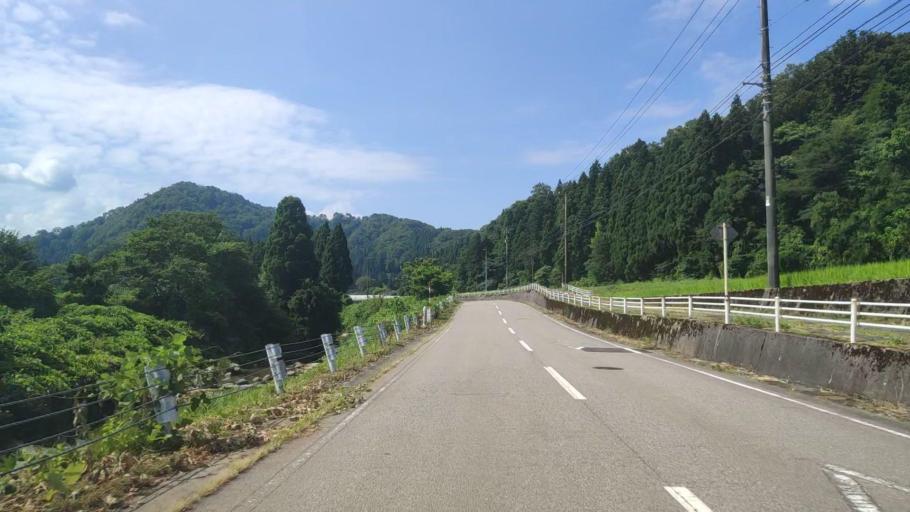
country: JP
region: Ishikawa
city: Komatsu
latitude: 36.3320
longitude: 136.5274
